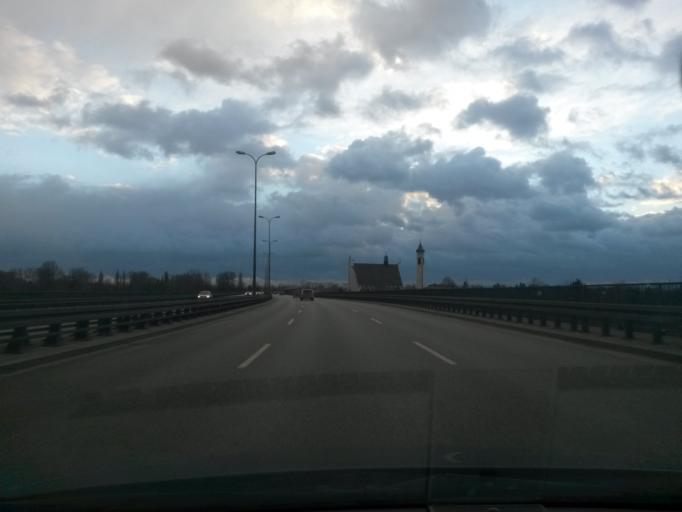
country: PL
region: Masovian Voivodeship
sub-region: Warszawa
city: Praga Poludnie
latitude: 52.2111
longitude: 21.0874
